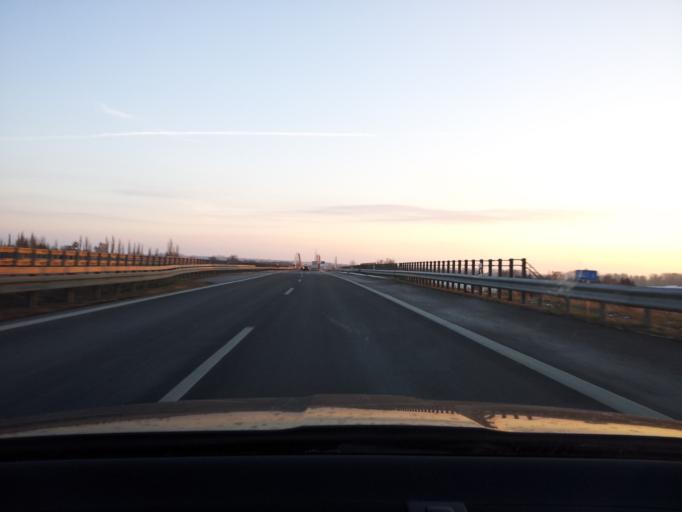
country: DE
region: Brandenburg
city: Brieselang
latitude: 52.5915
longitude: 12.9706
